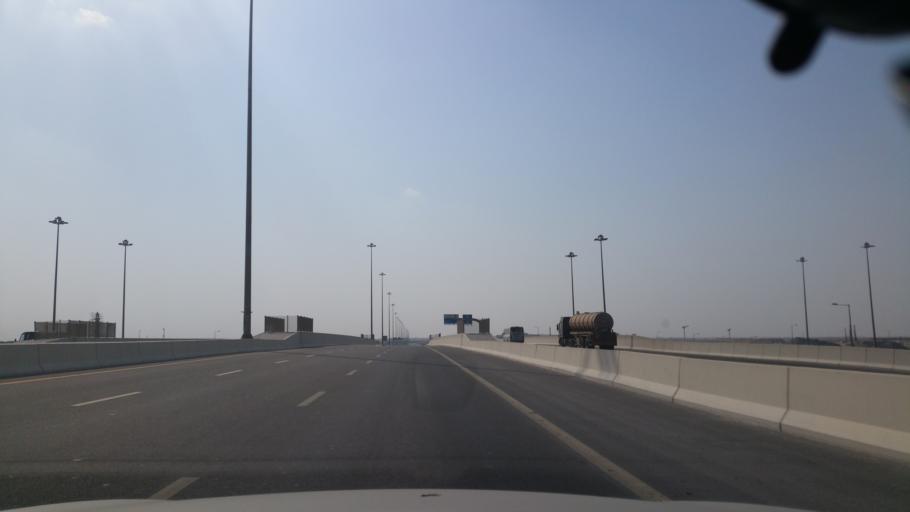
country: QA
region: Baladiyat Umm Salal
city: Umm Salal `Ali
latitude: 25.4570
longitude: 51.4795
